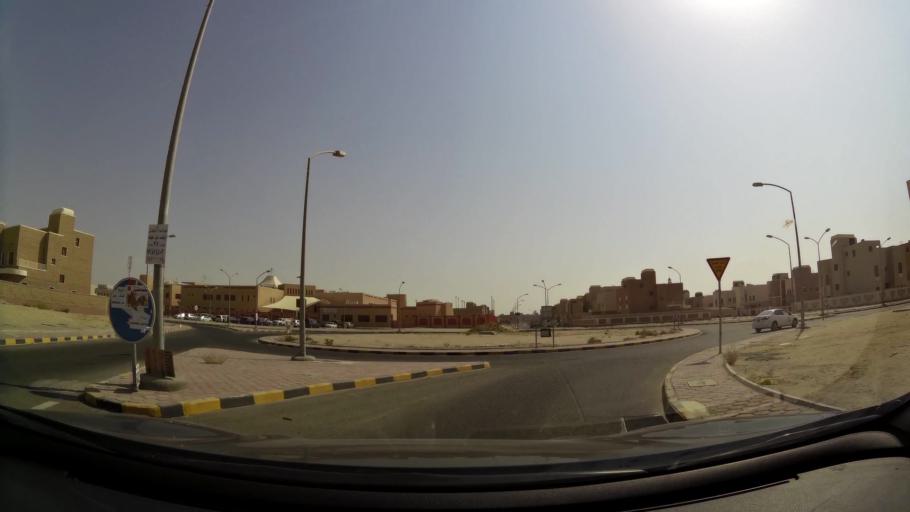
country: KW
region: Al Ahmadi
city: Al Wafrah
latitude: 28.8047
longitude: 48.0535
